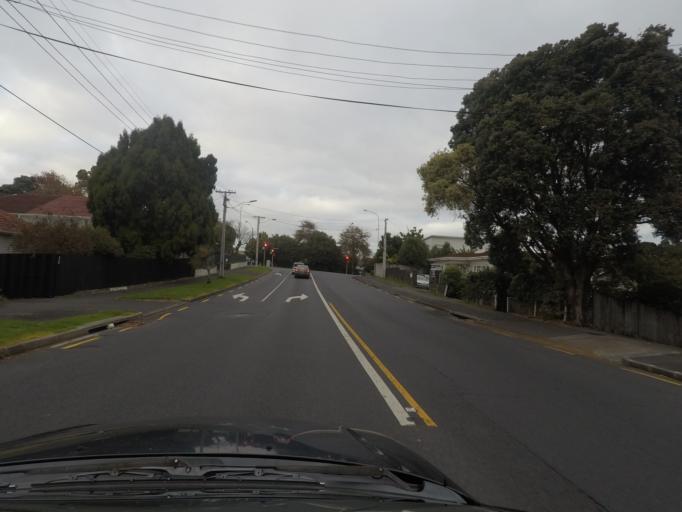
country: NZ
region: Auckland
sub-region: Auckland
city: Auckland
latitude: -36.8883
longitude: 174.7704
